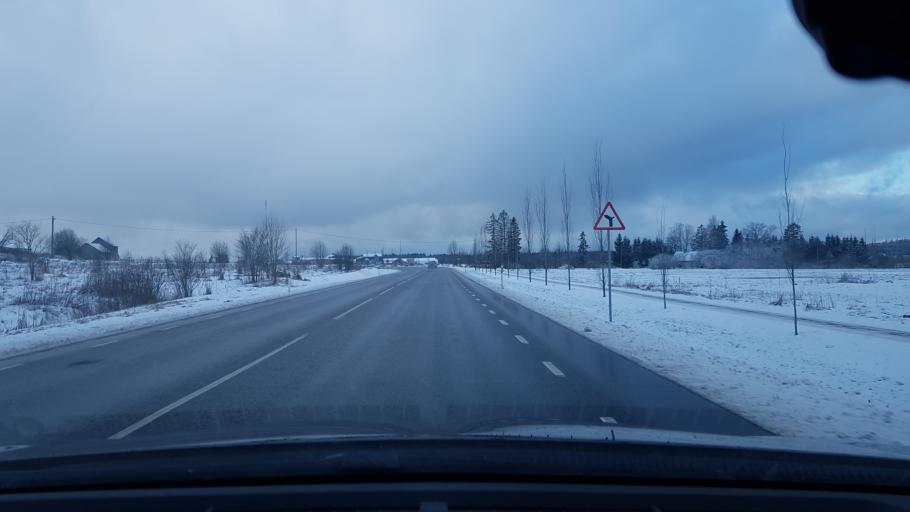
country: EE
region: Harju
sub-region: Paldiski linn
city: Paldiski
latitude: 59.2281
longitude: 24.1358
